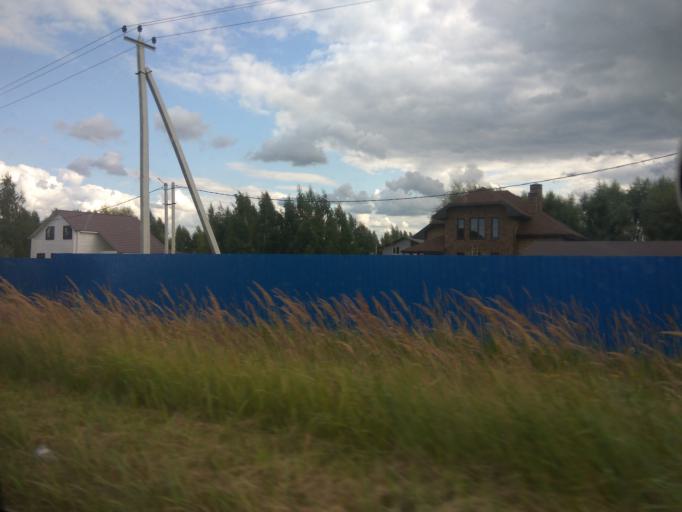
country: RU
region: Moskovskaya
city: Bronnitsy
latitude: 55.4574
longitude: 38.2461
